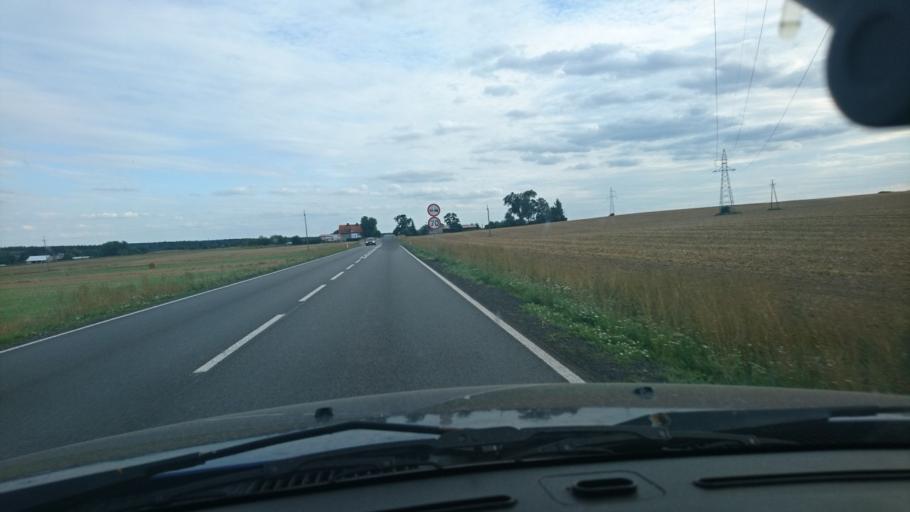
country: PL
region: Greater Poland Voivodeship
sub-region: Powiat ostrzeszowski
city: Ostrzeszow
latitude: 51.3630
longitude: 17.9461
